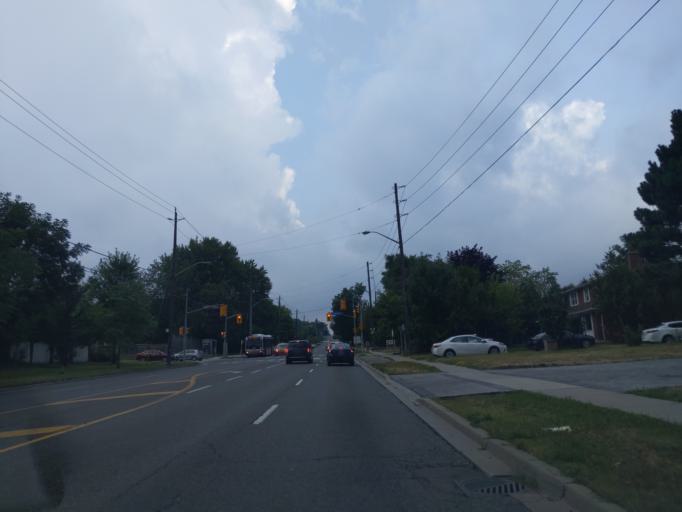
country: CA
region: Ontario
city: Willowdale
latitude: 43.8025
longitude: -79.4001
